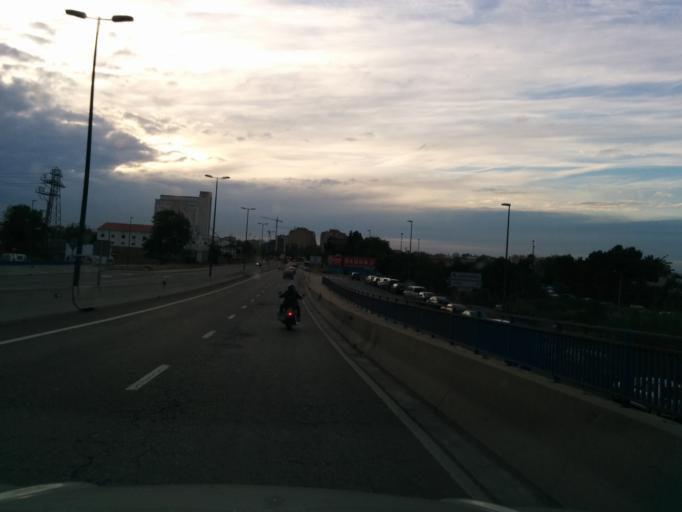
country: ES
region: Aragon
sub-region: Provincia de Zaragoza
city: Zaragoza
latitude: 41.6311
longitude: -0.8576
